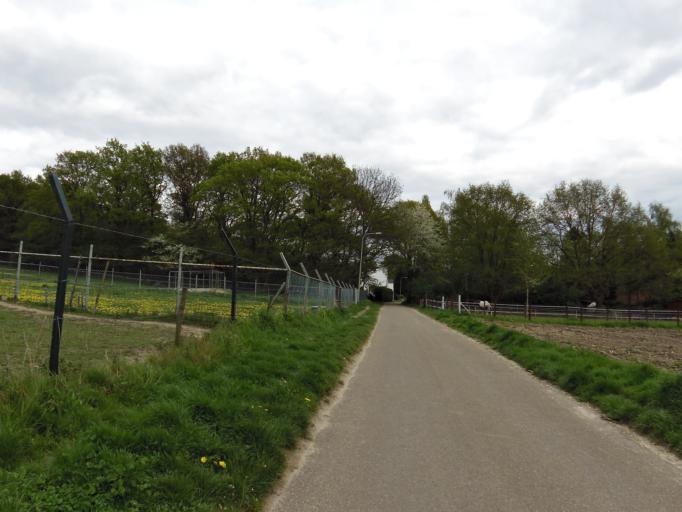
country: NL
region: Limburg
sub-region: Gemeente Heerlen
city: Heerlen
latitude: 50.9123
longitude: 6.0134
